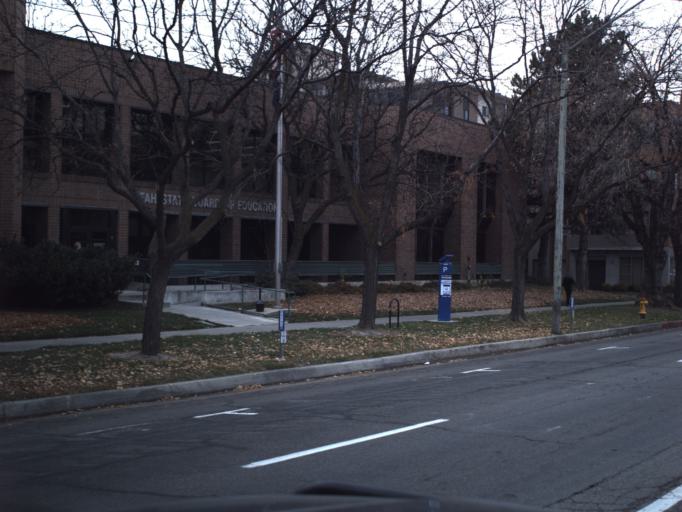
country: US
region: Utah
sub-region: Salt Lake County
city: Salt Lake City
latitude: 40.7585
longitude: -111.8835
